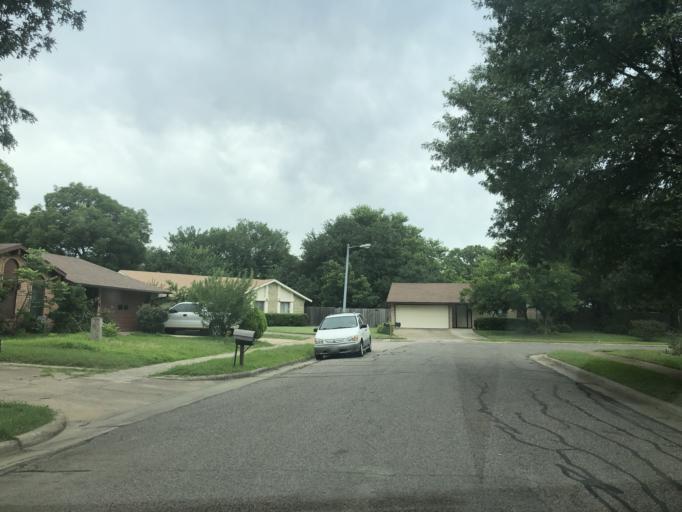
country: US
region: Texas
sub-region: Dallas County
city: Irving
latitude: 32.7916
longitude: -96.9827
